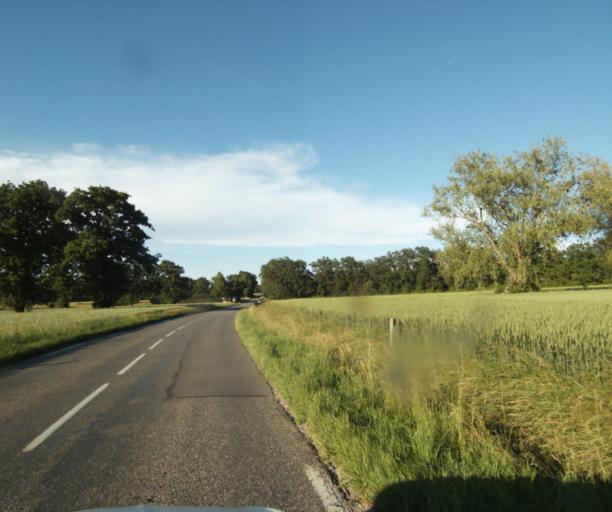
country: FR
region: Rhone-Alpes
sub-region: Departement de la Haute-Savoie
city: Messery
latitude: 46.3563
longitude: 6.3047
